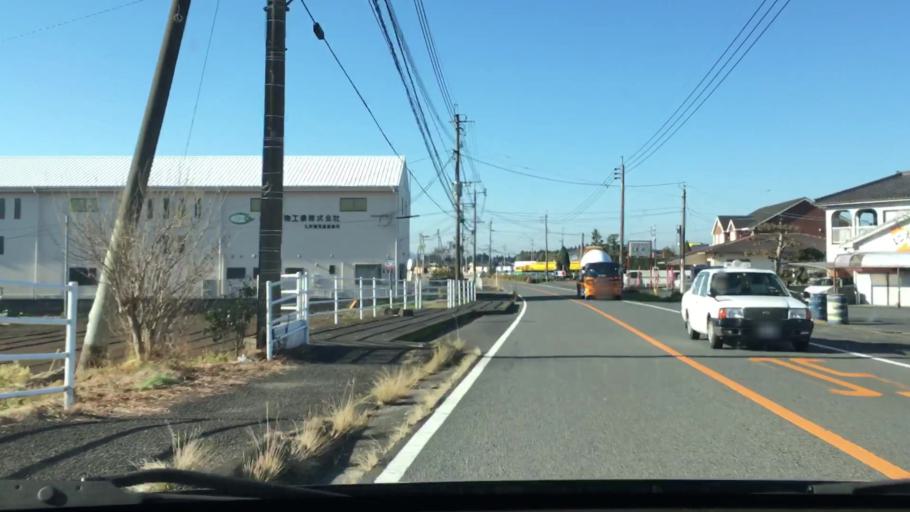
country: JP
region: Kagoshima
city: Kajiki
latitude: 31.7872
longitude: 130.7082
